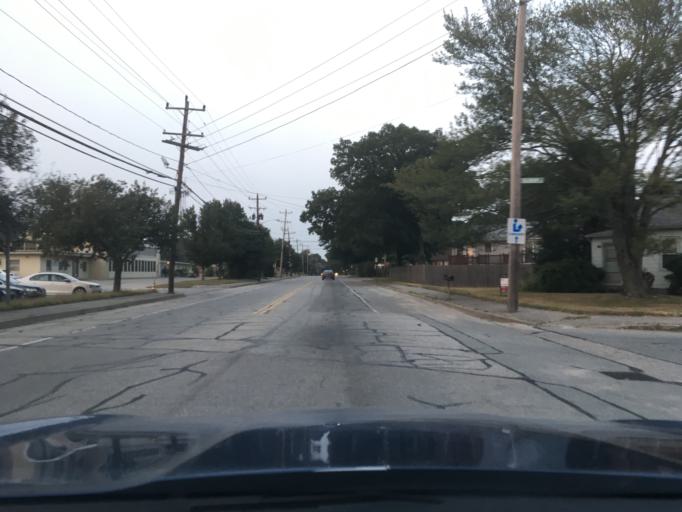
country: US
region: Rhode Island
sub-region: Kent County
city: Warwick
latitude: 41.7068
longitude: -71.4150
